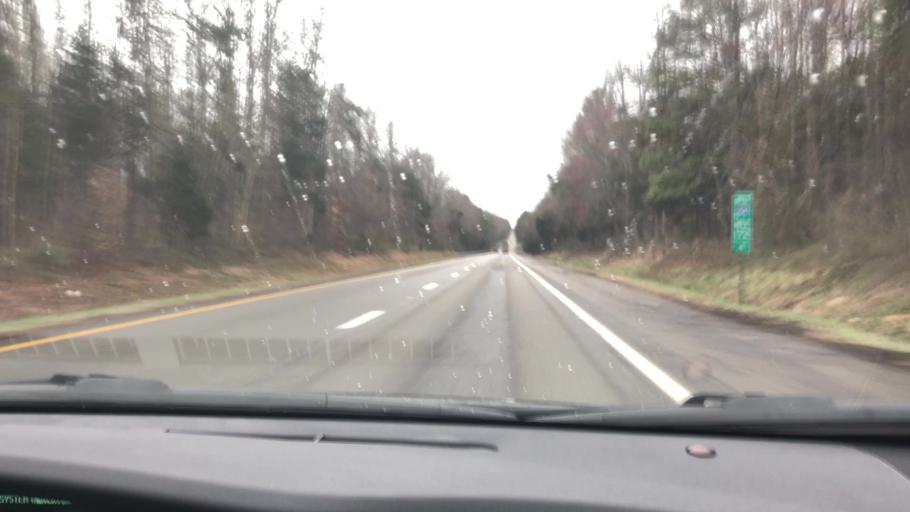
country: US
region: Virginia
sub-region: Henrico County
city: Wyndham
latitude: 37.6902
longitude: -77.6923
